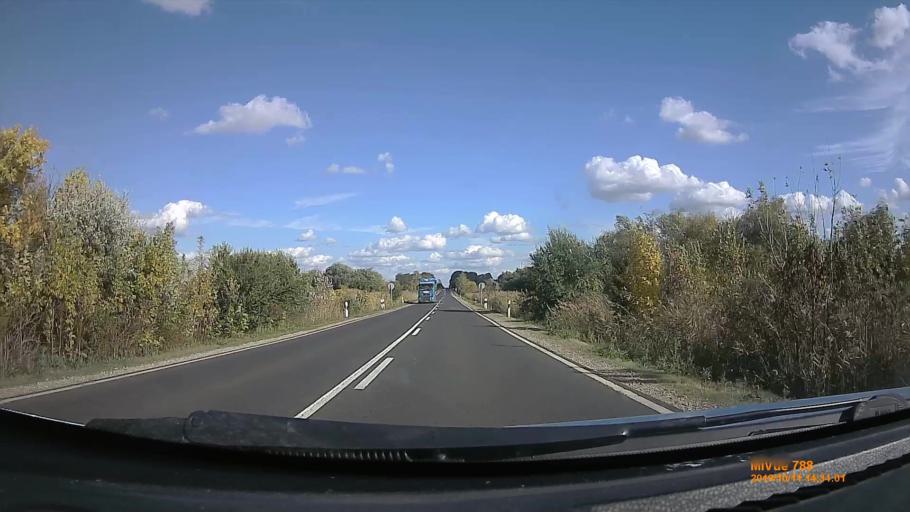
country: HU
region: Hajdu-Bihar
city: Ebes
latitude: 47.5610
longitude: 21.4668
